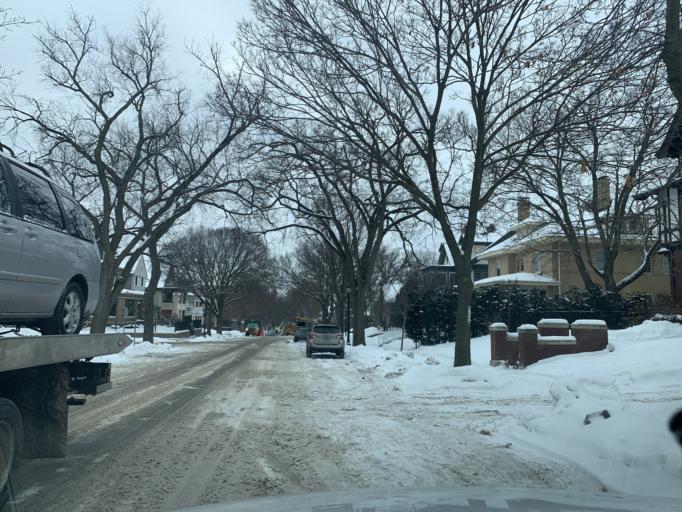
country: US
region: Minnesota
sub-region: Hennepin County
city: Minneapolis
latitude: 44.9649
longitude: -93.2957
